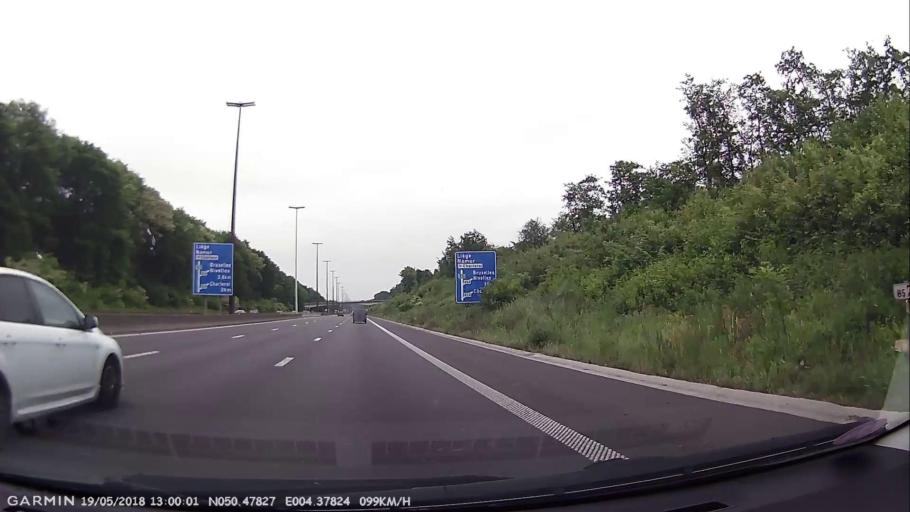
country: BE
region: Wallonia
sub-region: Province du Hainaut
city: Courcelles
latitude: 50.4782
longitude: 4.3785
